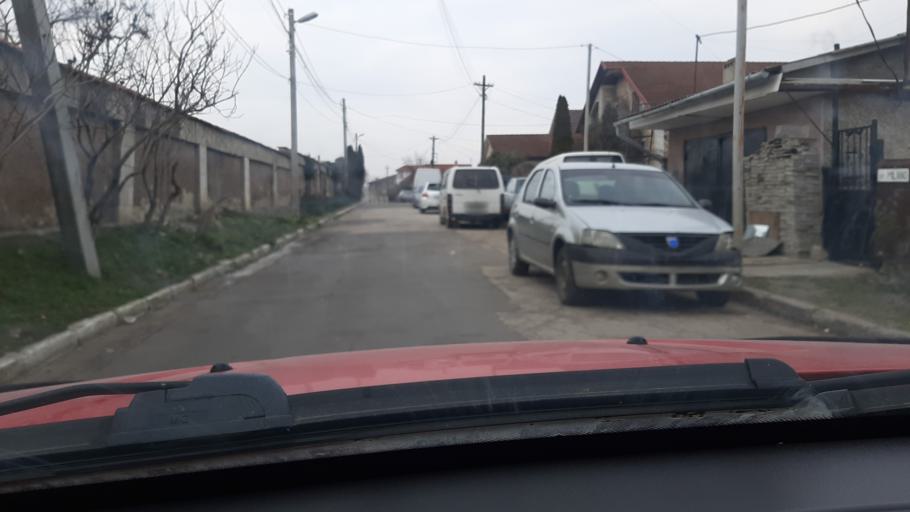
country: MD
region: Chisinau
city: Chisinau
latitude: 47.0364
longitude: 28.7986
